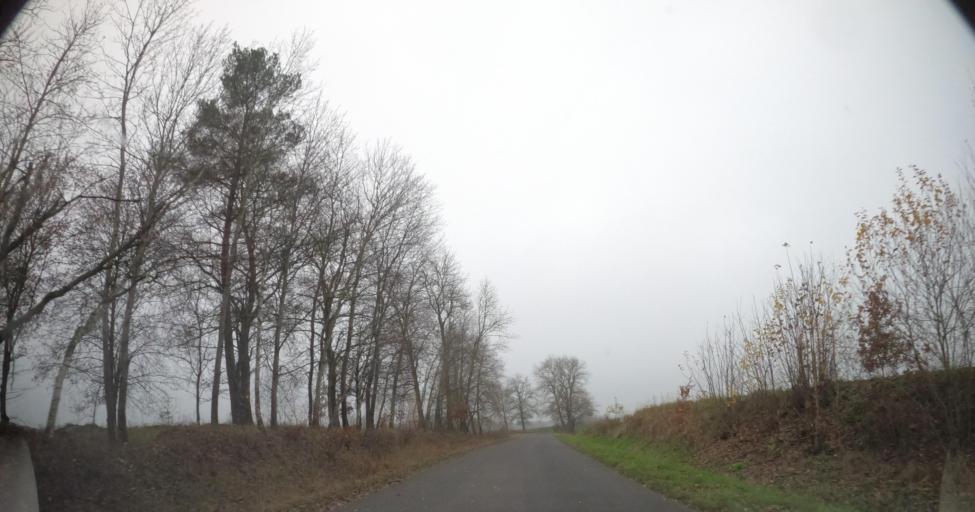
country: PL
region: West Pomeranian Voivodeship
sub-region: Powiat drawski
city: Drawsko Pomorskie
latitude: 53.6002
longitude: 15.7347
